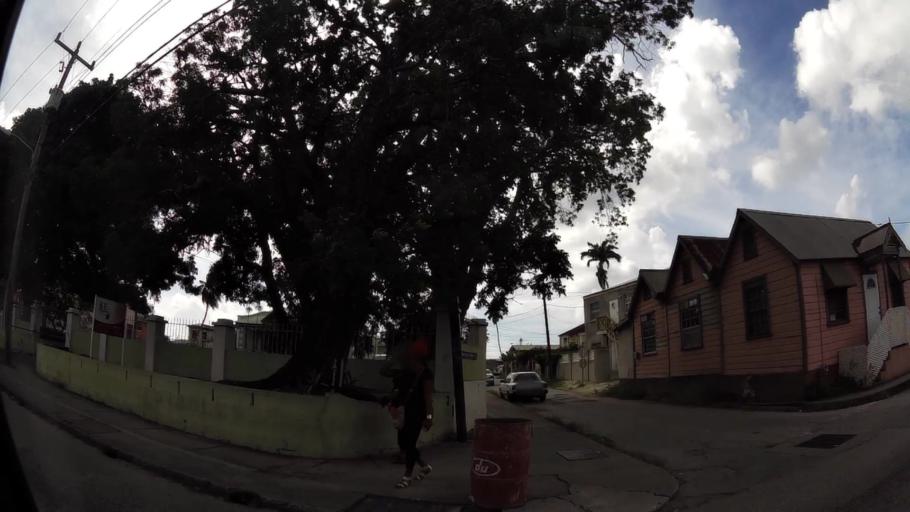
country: BB
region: Saint Michael
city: Bridgetown
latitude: 13.0955
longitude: -59.6086
